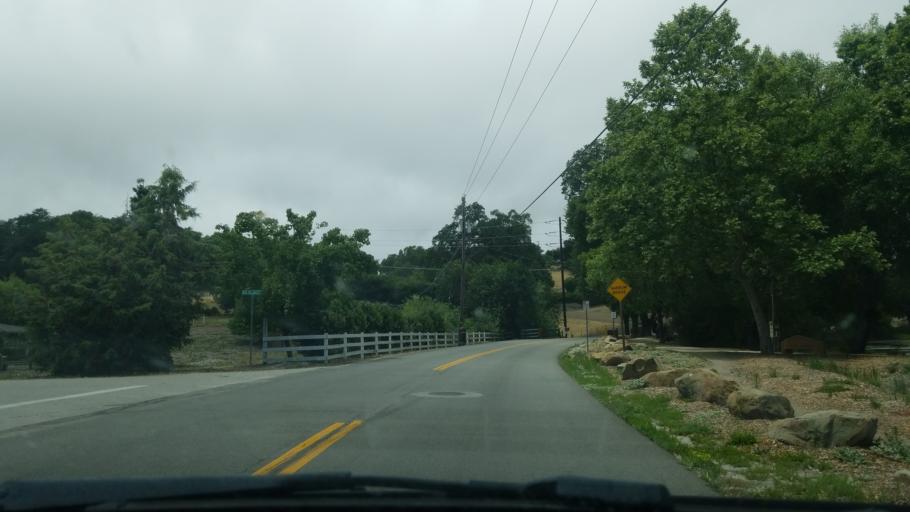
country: US
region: California
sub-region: San Luis Obispo County
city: Atascadero
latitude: 35.4617
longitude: -120.6636
